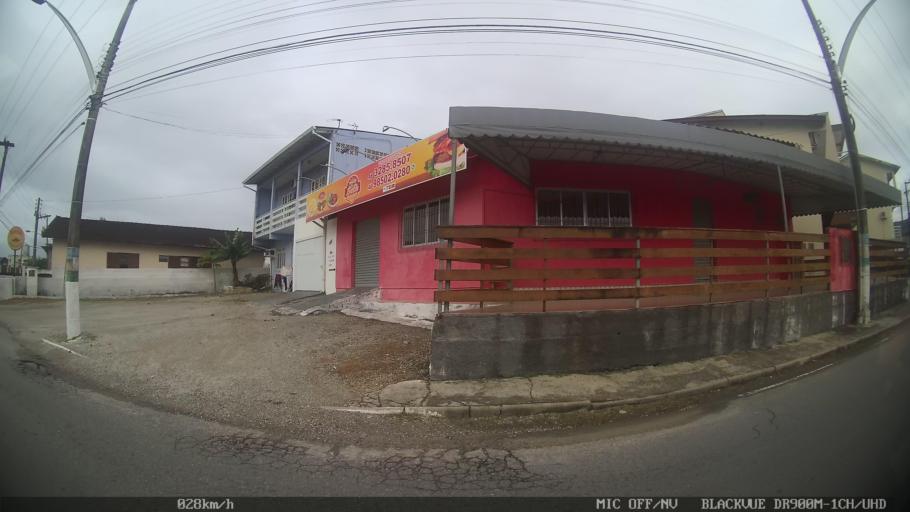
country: BR
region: Santa Catarina
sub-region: Biguacu
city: Biguacu
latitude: -27.5314
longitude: -48.6360
